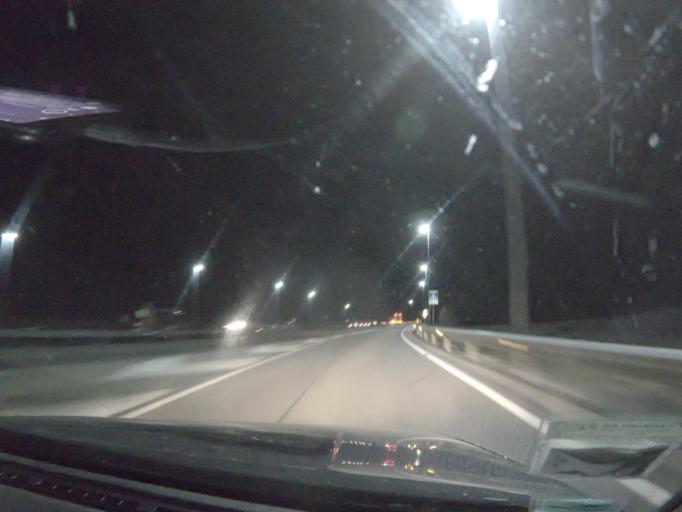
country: ES
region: Castille and Leon
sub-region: Provincia de Zamora
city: Pobladura del Valle
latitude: 42.0872
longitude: -5.7142
